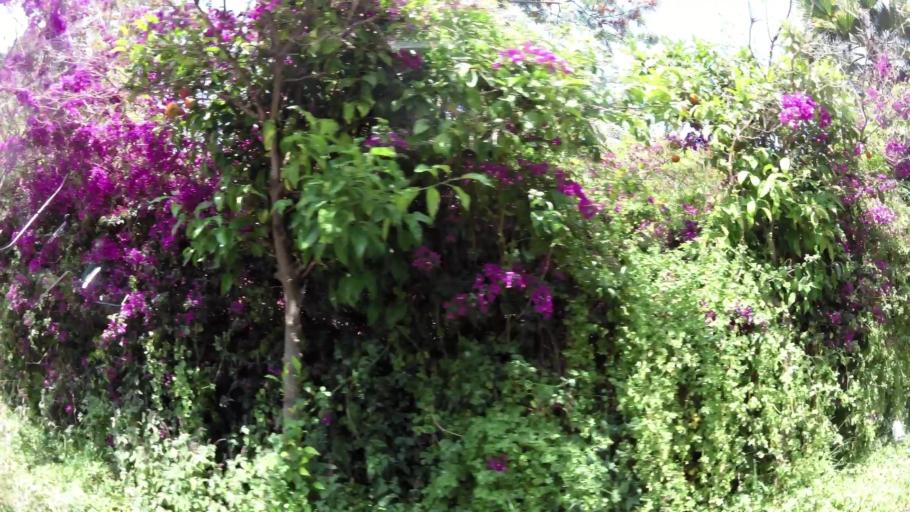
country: MA
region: Rabat-Sale-Zemmour-Zaer
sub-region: Rabat
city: Rabat
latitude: 33.9785
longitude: -6.8386
